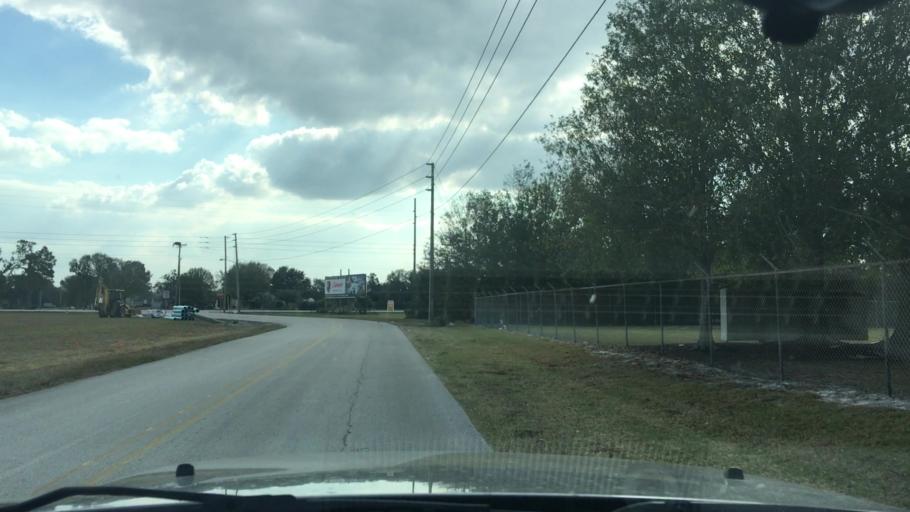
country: US
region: Florida
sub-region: Highlands County
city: Sebring
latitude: 27.4357
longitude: -81.3629
